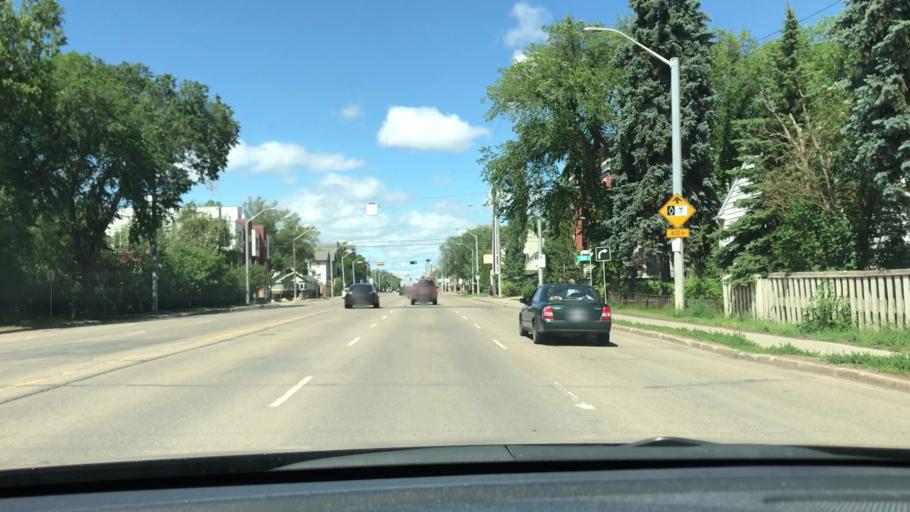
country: CA
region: Alberta
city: Edmonton
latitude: 53.5147
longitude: -113.5120
